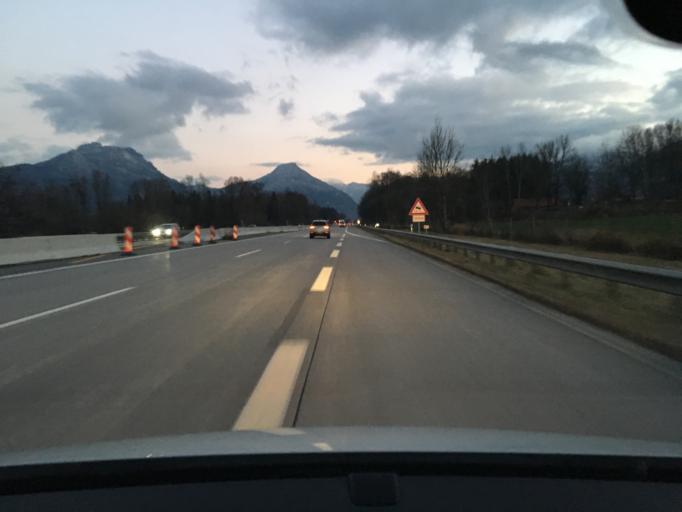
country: DE
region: Bavaria
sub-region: Upper Bavaria
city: Brannenburg
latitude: 47.7581
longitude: 12.1092
